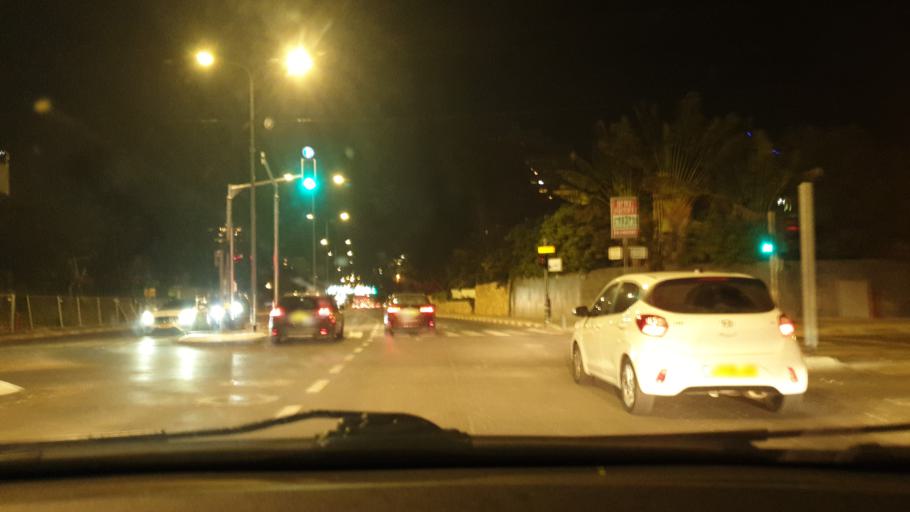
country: IL
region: Tel Aviv
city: Ramat Gan
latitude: 32.1209
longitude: 34.8051
